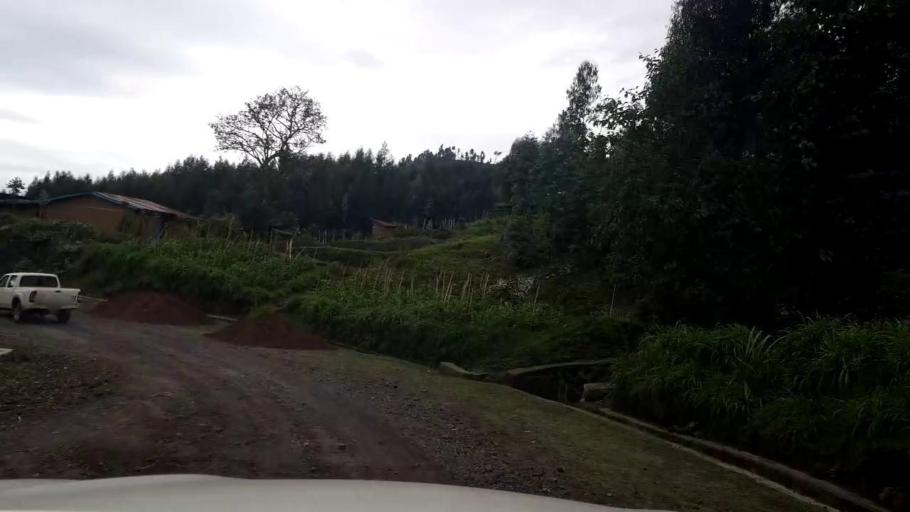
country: RW
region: Northern Province
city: Musanze
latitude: -1.5078
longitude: 29.5323
